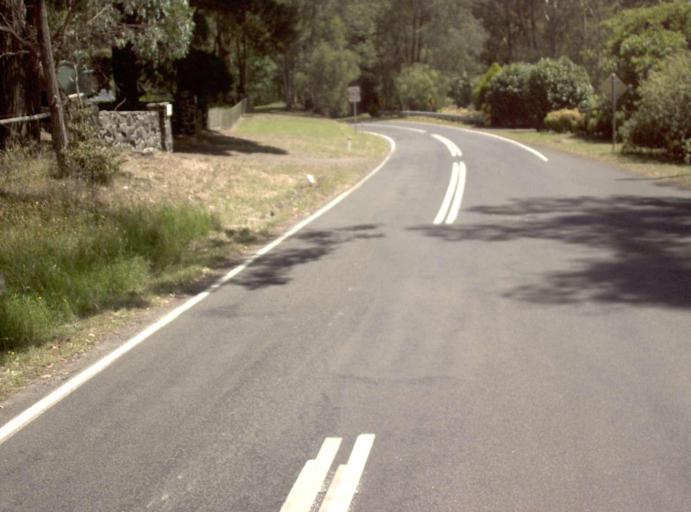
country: AU
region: Victoria
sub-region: Baw Baw
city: Warragul
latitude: -37.8986
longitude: 146.0245
